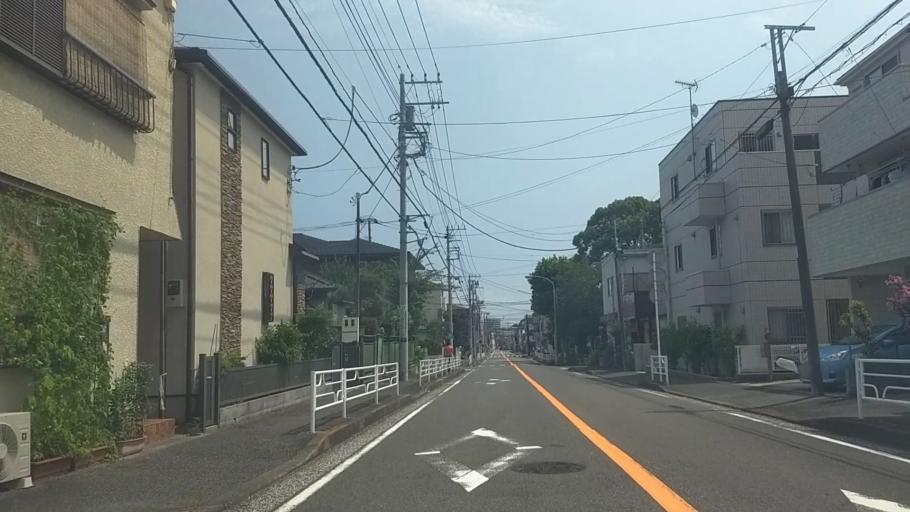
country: JP
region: Kanagawa
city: Yokohama
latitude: 35.4922
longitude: 139.6411
